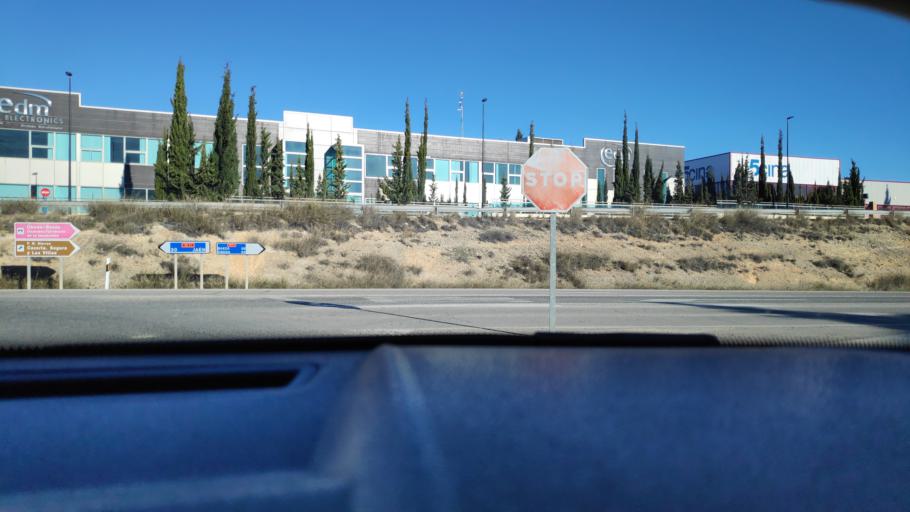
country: ES
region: Andalusia
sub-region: Provincia de Jaen
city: Mancha Real
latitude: 37.8070
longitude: -3.6121
